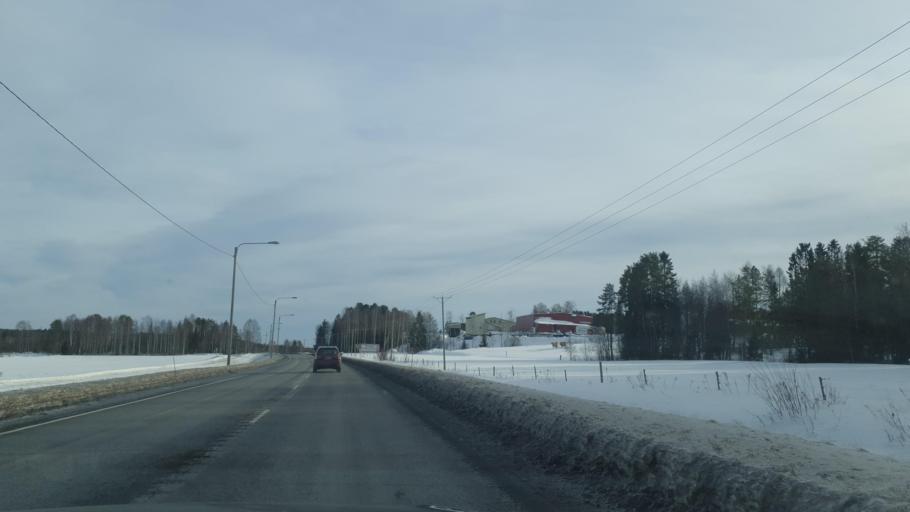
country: FI
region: Northern Ostrobothnia
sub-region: Oulu
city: Muhos
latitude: 64.8890
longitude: 25.8164
